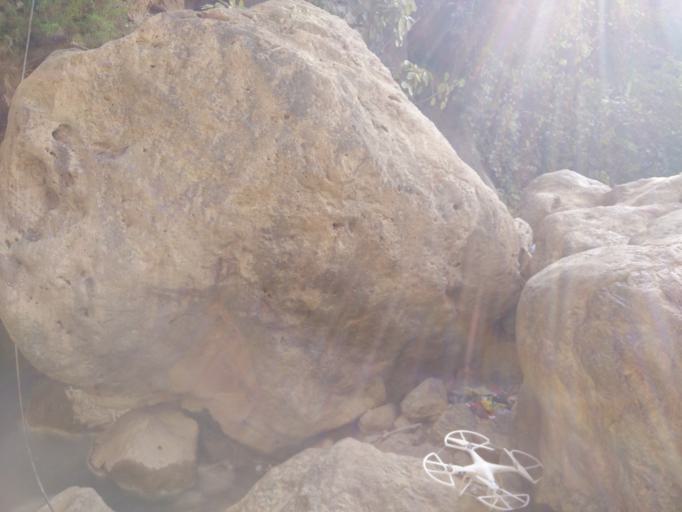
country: MM
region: Mandalay
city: Kyaukse
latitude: 21.7112
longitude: 96.3554
